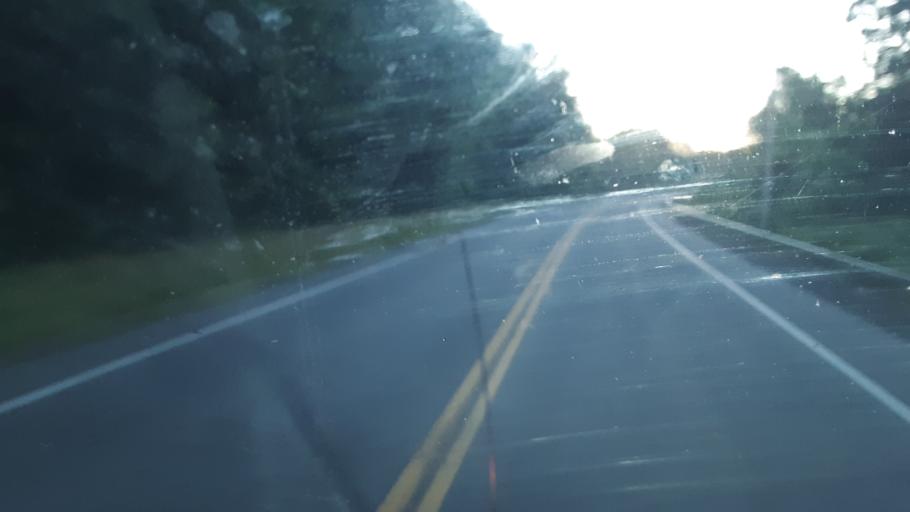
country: US
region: New York
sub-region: Schenectady County
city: East Glenville
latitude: 42.9756
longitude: -73.9682
